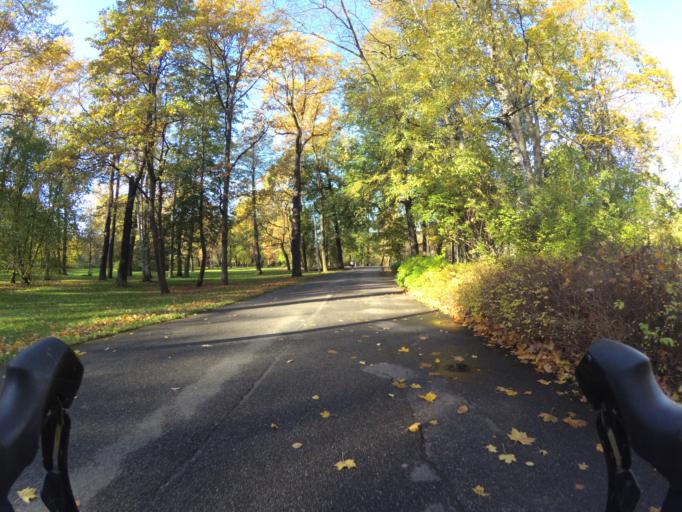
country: RU
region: Leningrad
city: Krestovskiy ostrov
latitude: 59.9800
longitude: 30.2625
